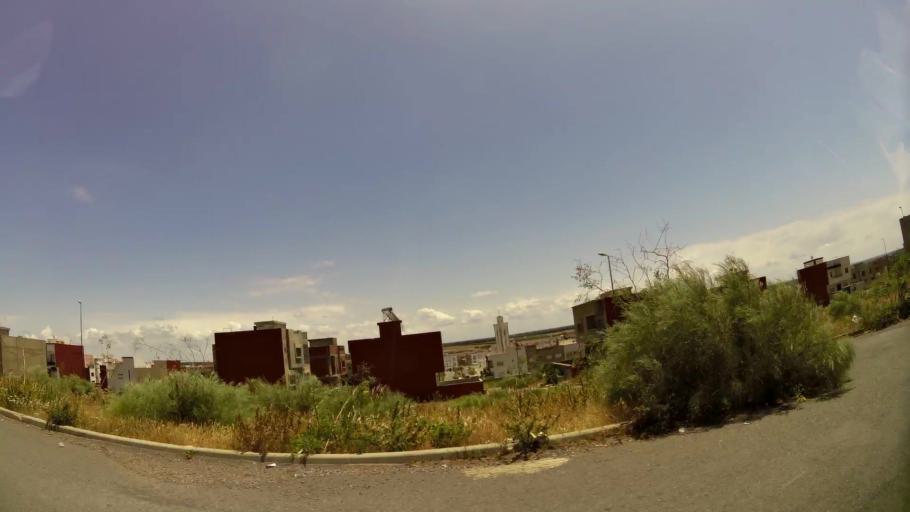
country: MA
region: Gharb-Chrarda-Beni Hssen
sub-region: Kenitra Province
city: Kenitra
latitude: 34.2511
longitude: -6.6595
